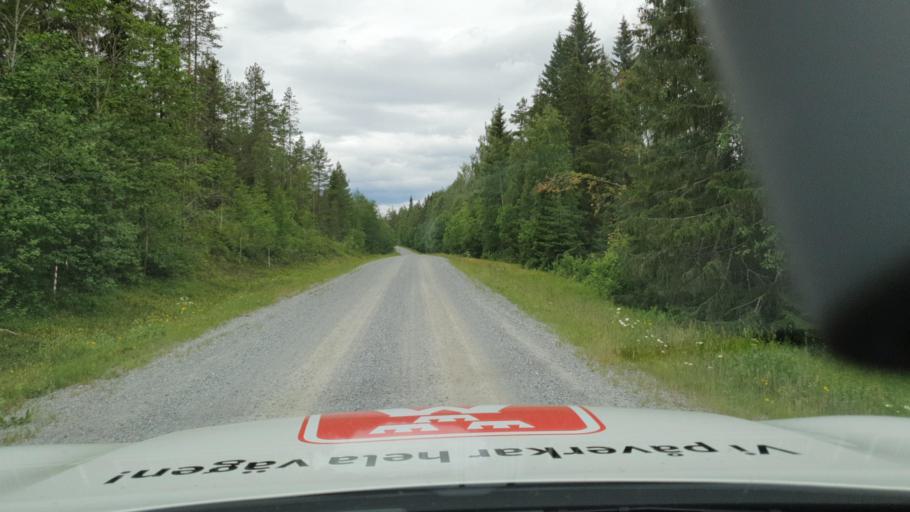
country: SE
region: Vaesterbotten
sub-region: Nordmalings Kommun
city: Nordmaling
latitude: 63.7349
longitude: 19.4190
